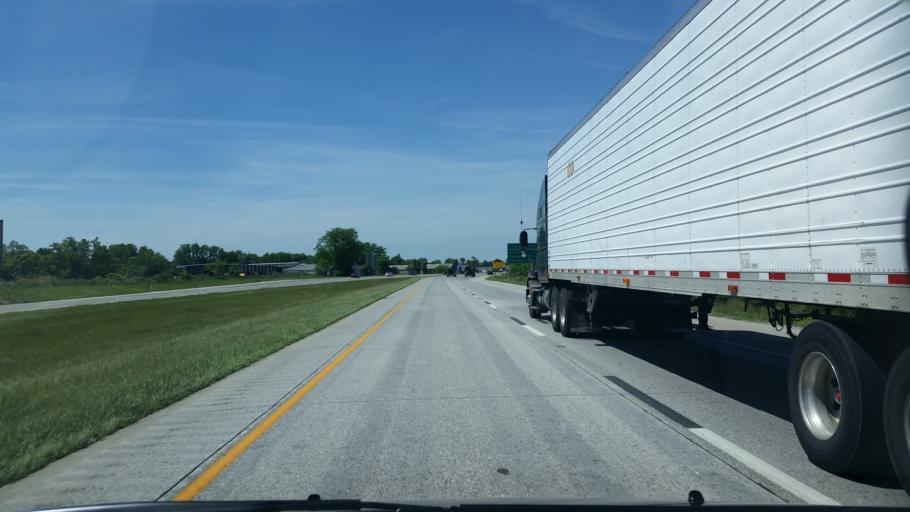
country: US
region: Pennsylvania
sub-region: Cumberland County
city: Schlusser
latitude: 40.2266
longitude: -77.1365
